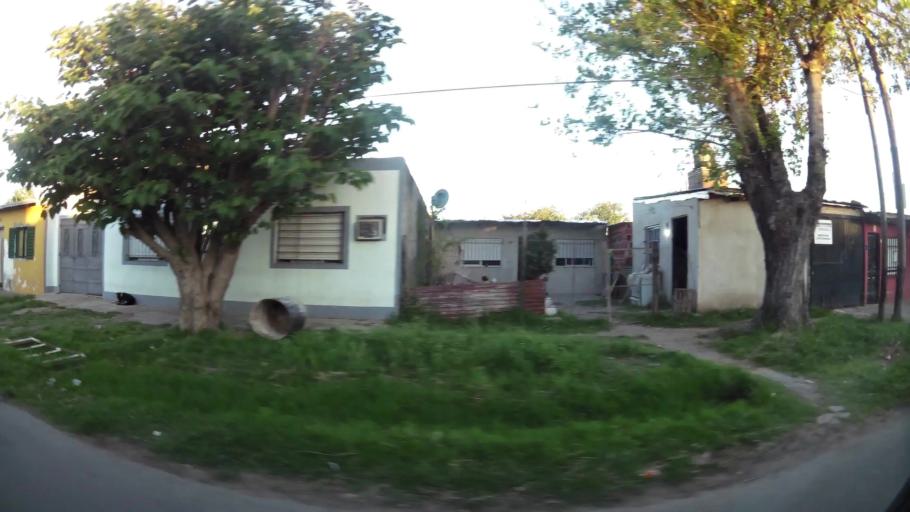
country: AR
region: Santa Fe
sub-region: Departamento de Rosario
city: Rosario
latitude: -32.9622
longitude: -60.6821
